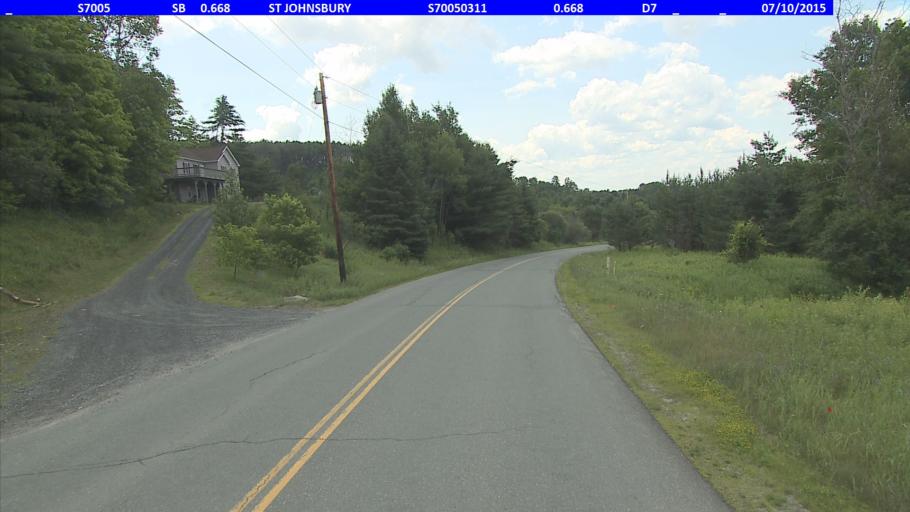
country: US
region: Vermont
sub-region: Caledonia County
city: St Johnsbury
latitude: 44.4433
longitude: -72.0053
